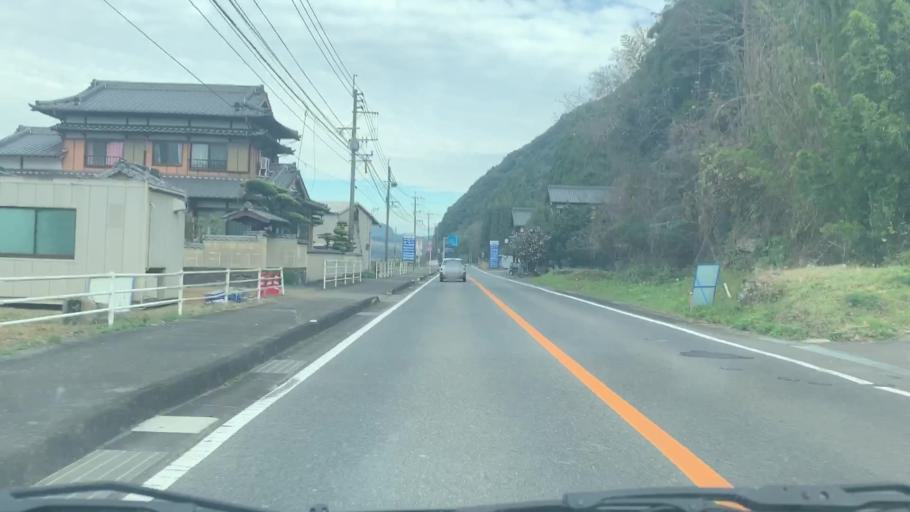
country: JP
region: Saga Prefecture
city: Imaricho-ko
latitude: 33.2686
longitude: 129.9644
